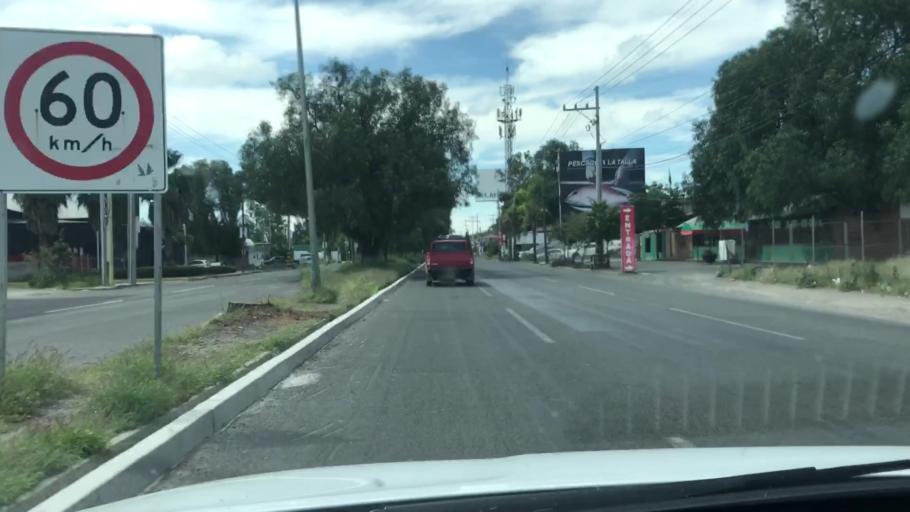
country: MX
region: Guanajuato
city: Celaya
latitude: 20.5256
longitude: -100.7778
